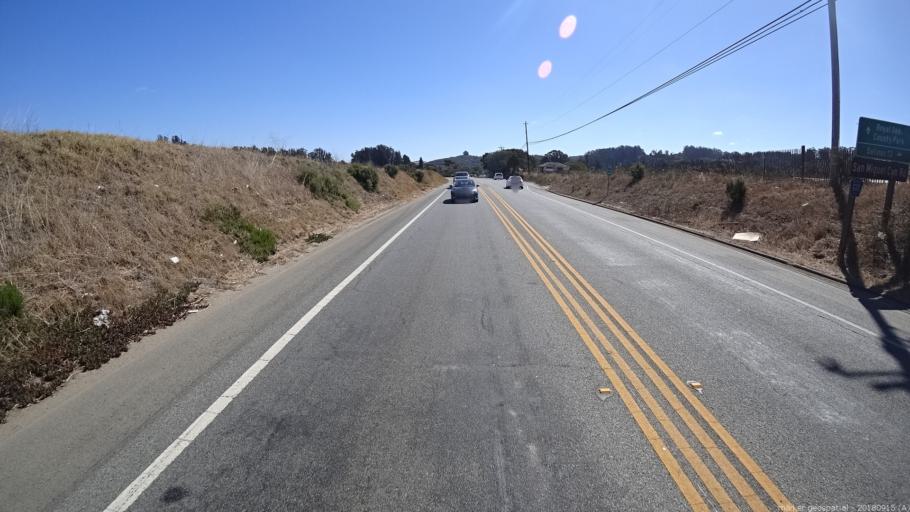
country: US
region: California
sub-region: Monterey County
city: Las Lomas
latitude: 36.8598
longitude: -121.6967
